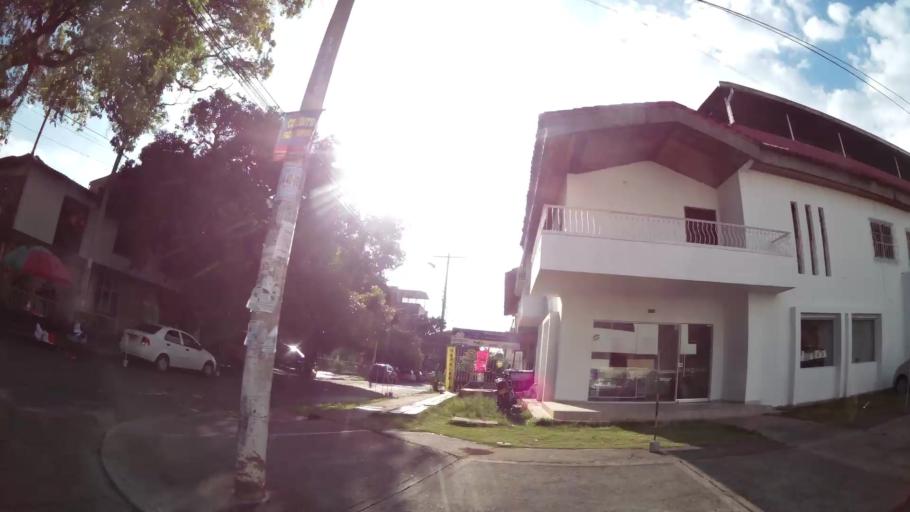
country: CO
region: Valle del Cauca
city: Cali
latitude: 3.4201
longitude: -76.5462
